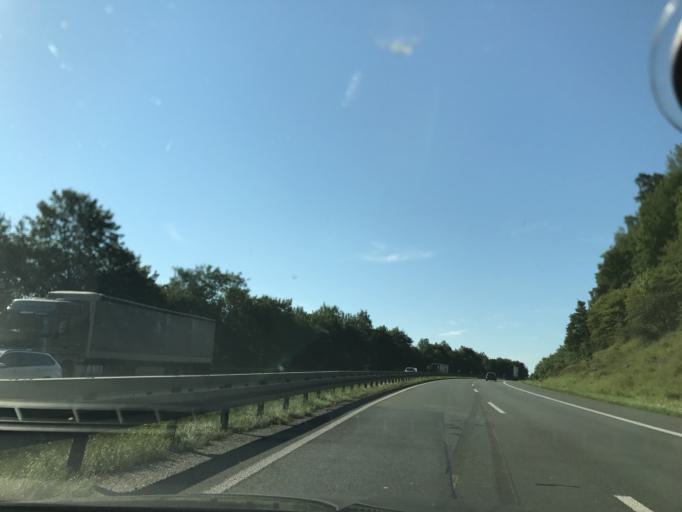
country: DE
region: Hesse
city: Herborn
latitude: 50.6934
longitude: 8.2952
